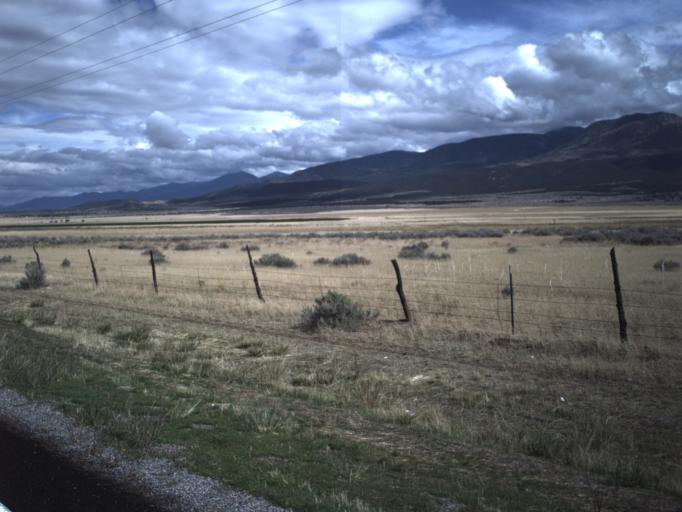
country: US
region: Utah
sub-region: Millard County
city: Fillmore
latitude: 38.8208
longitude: -112.4336
